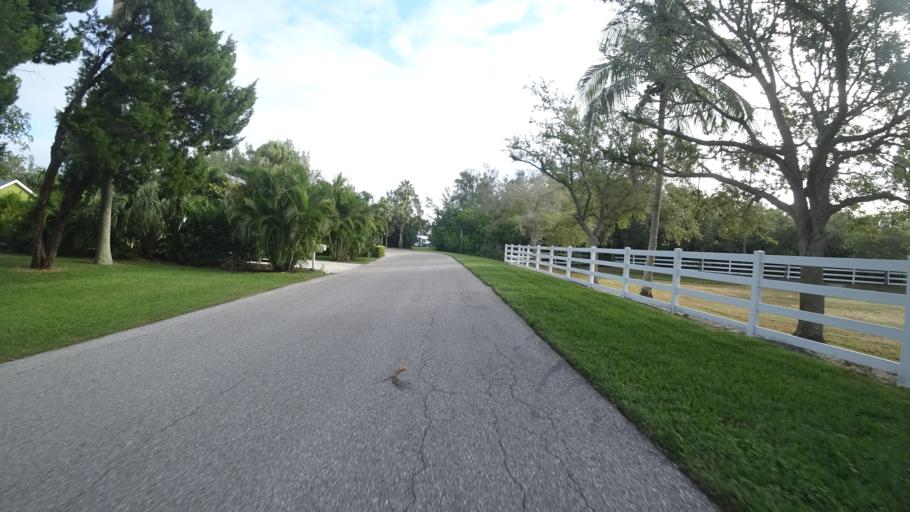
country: US
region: Florida
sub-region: Manatee County
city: Cortez
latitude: 27.4381
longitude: -82.6864
